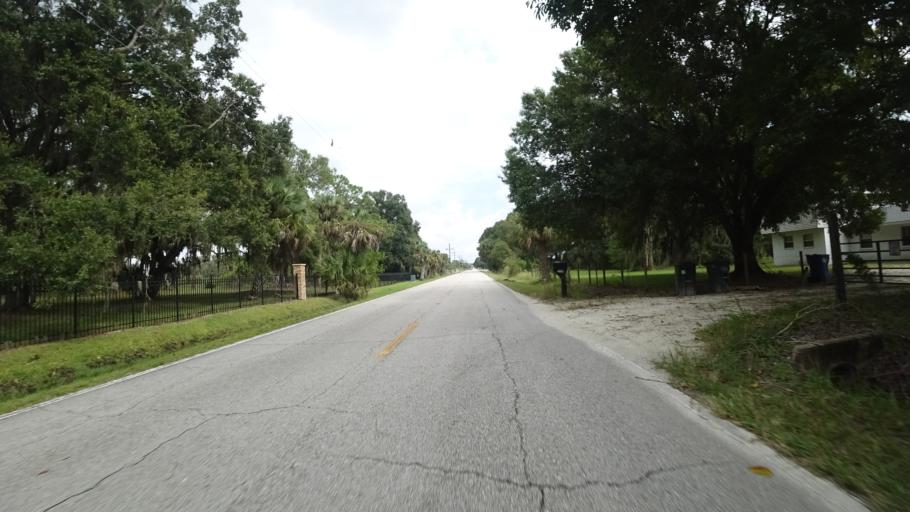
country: US
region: Florida
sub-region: Manatee County
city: Ellenton
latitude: 27.4879
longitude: -82.3898
